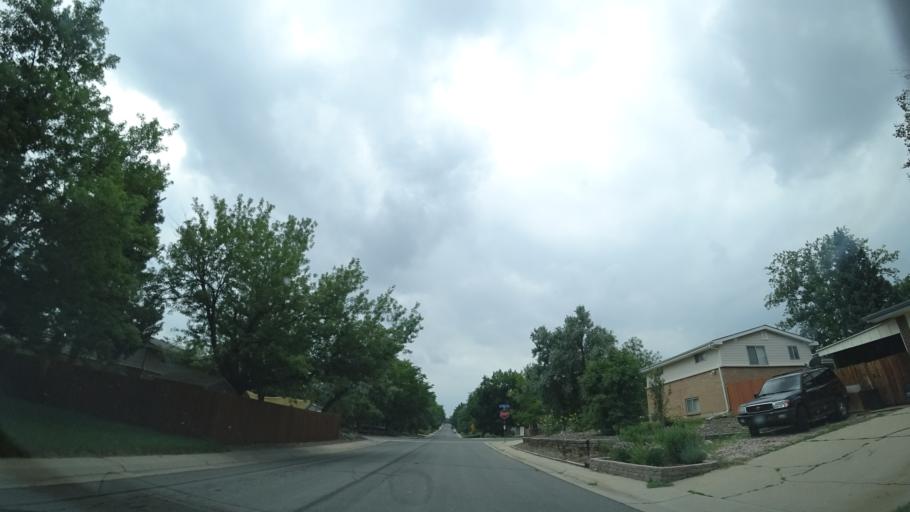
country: US
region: Colorado
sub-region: Jefferson County
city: West Pleasant View
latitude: 39.7029
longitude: -105.1488
